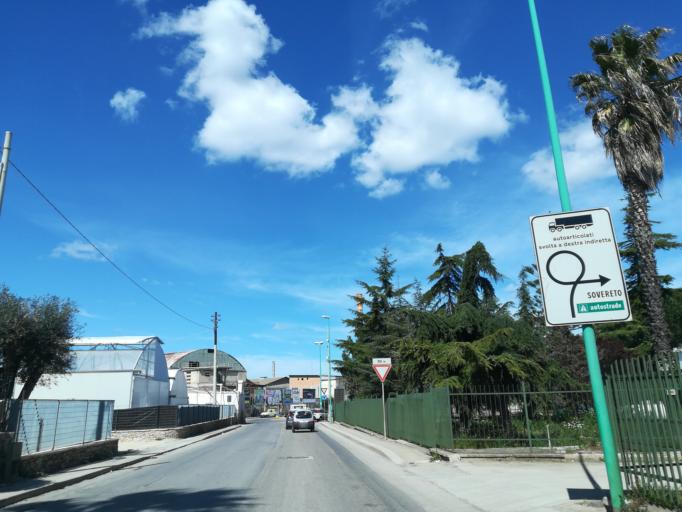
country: IT
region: Apulia
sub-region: Provincia di Bari
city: Terlizzi
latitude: 41.1241
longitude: 16.5478
